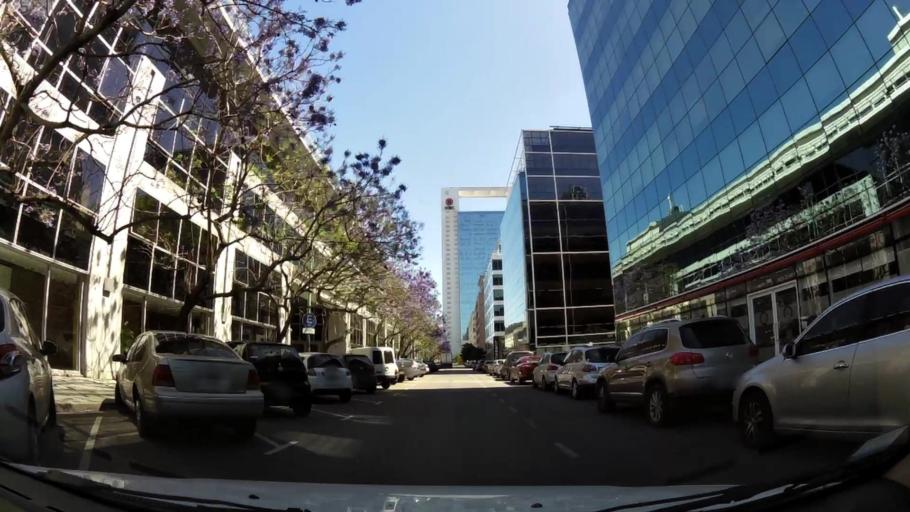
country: AR
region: Buenos Aires F.D.
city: Buenos Aires
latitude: -34.6019
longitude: -58.3644
